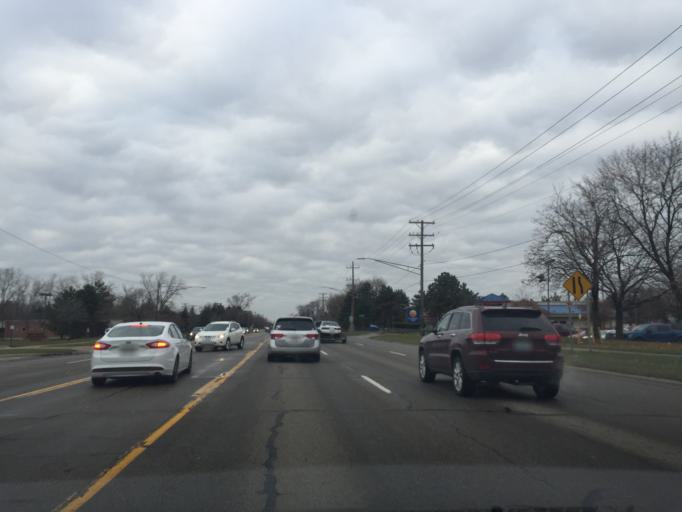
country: US
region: Michigan
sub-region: Wayne County
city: Livonia
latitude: 42.3847
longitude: -83.3337
